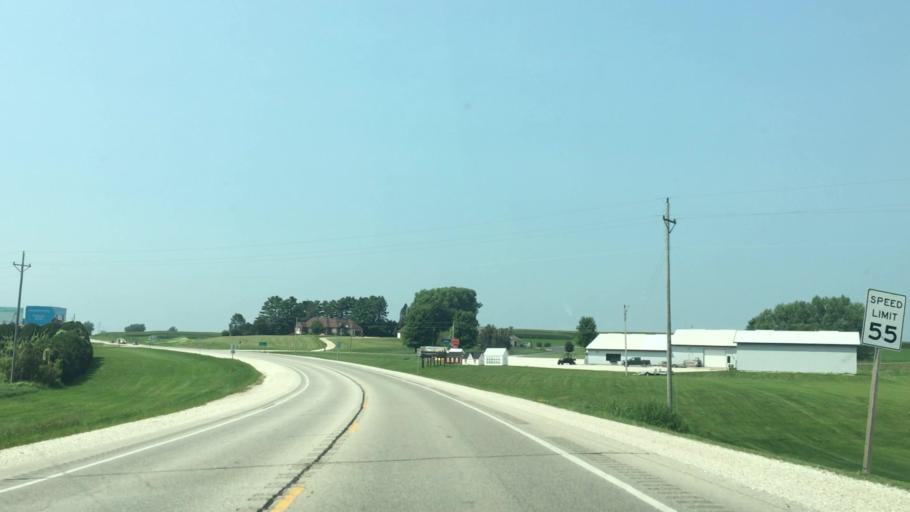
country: US
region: Iowa
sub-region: Winneshiek County
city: Decorah
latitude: 43.1885
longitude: -91.8645
